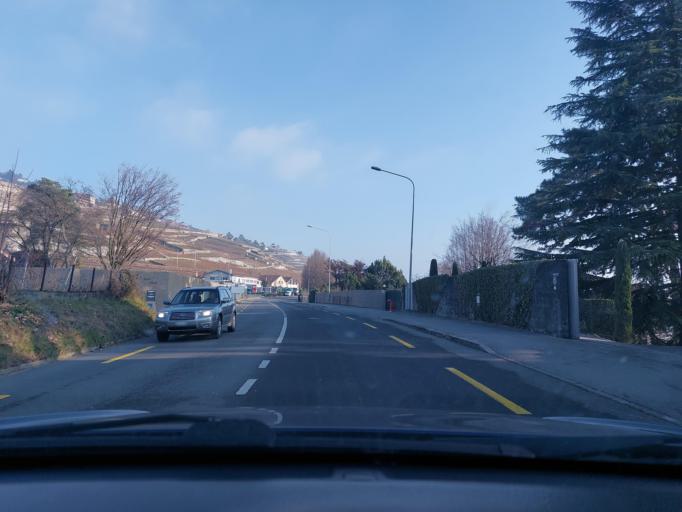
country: CH
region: Vaud
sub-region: Lavaux-Oron District
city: Lutry
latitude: 46.4990
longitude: 6.6988
